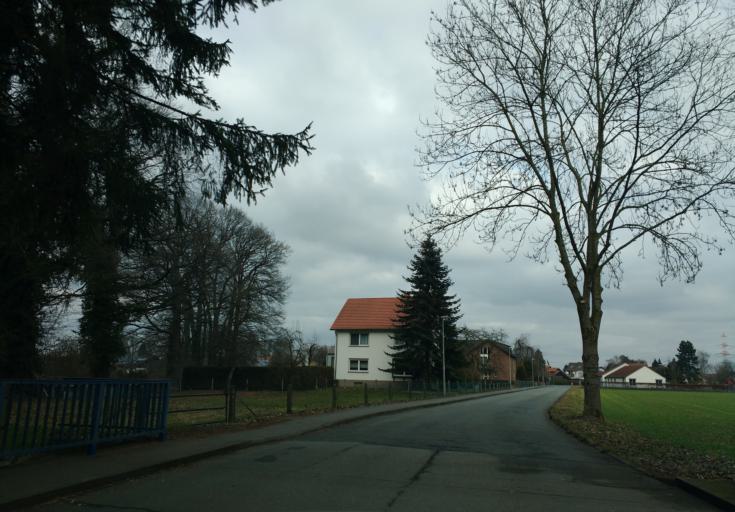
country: DE
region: North Rhine-Westphalia
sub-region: Regierungsbezirk Detmold
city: Paderborn
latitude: 51.7385
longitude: 8.6907
